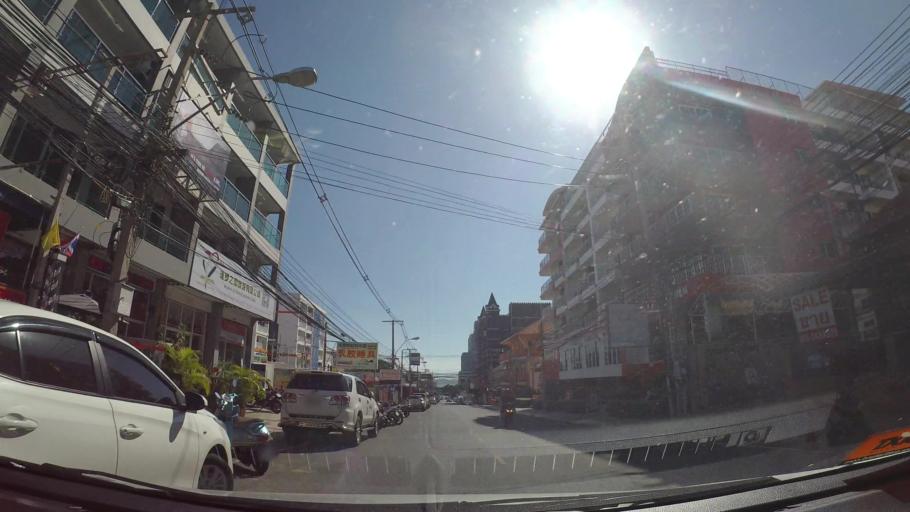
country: TH
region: Chon Buri
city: Phatthaya
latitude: 12.9152
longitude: 100.8630
